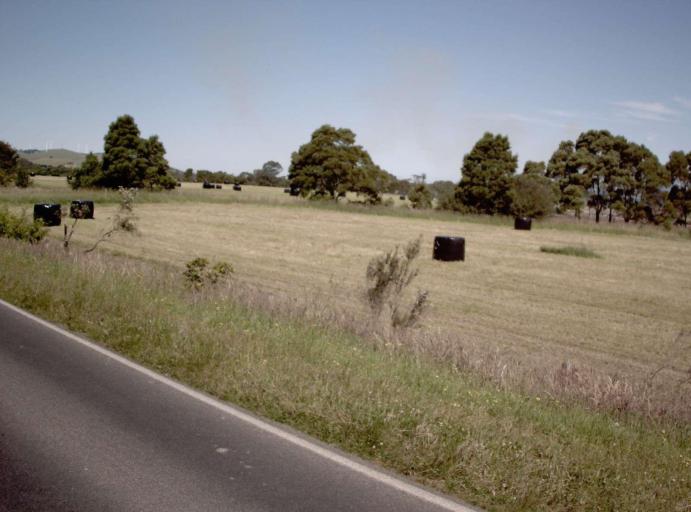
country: AU
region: Victoria
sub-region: Latrobe
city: Morwell
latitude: -38.6430
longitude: 146.2594
